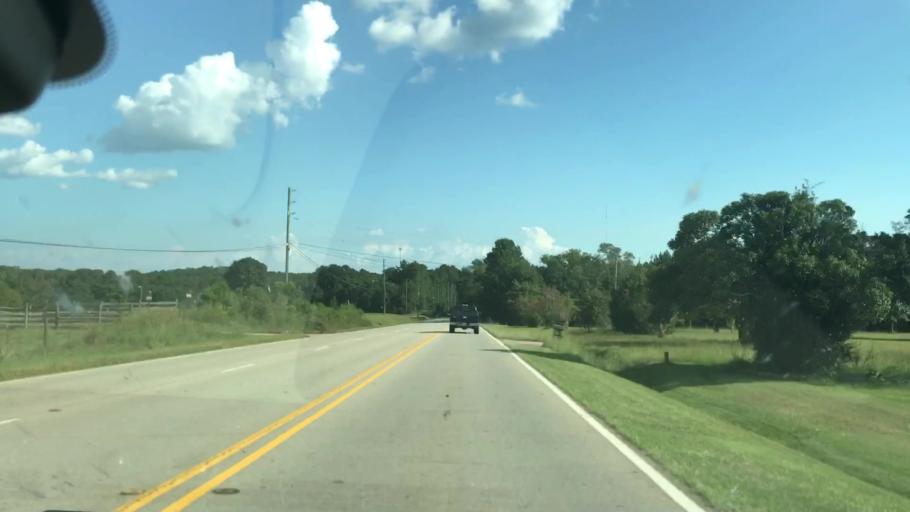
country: US
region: Georgia
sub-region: Troup County
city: La Grange
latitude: 32.9736
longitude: -84.9880
